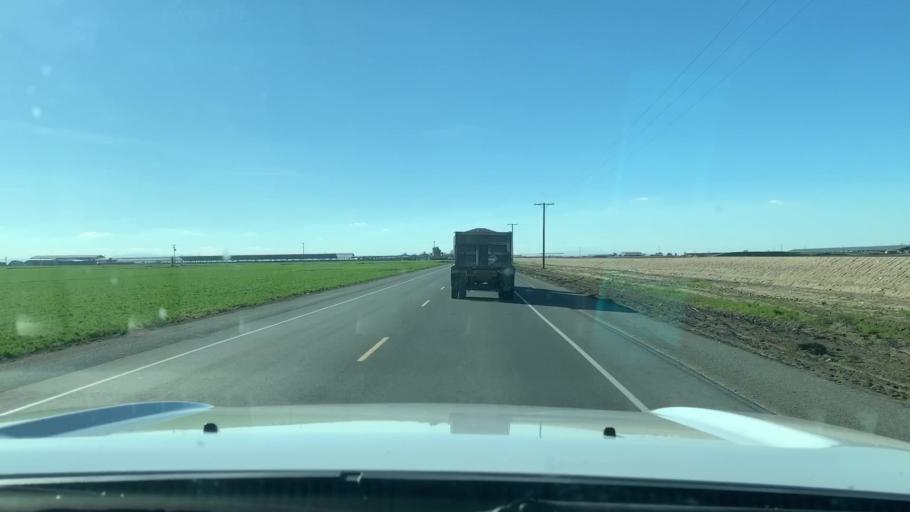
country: US
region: California
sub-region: Kings County
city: Corcoran
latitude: 36.2111
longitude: -119.5210
